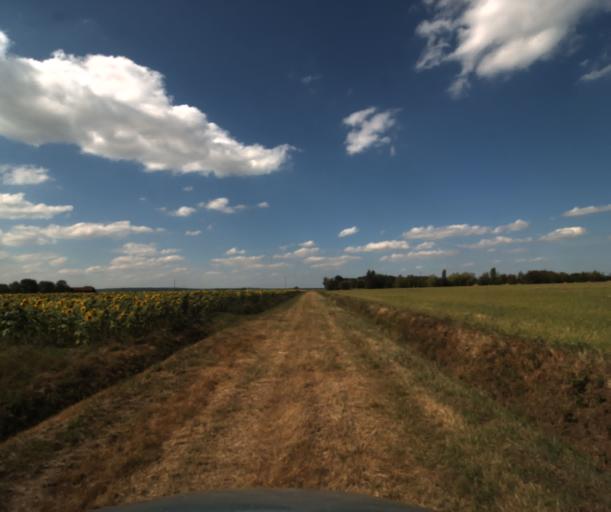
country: FR
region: Midi-Pyrenees
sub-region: Departement de la Haute-Garonne
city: Saint-Lys
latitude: 43.5268
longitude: 1.1788
